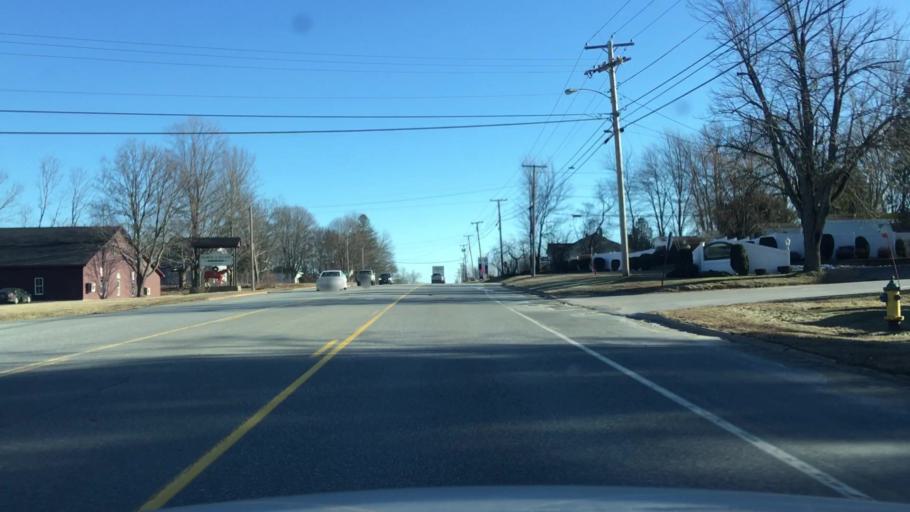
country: US
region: Maine
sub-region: Penobscot County
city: Holden
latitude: 44.7657
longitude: -68.7084
